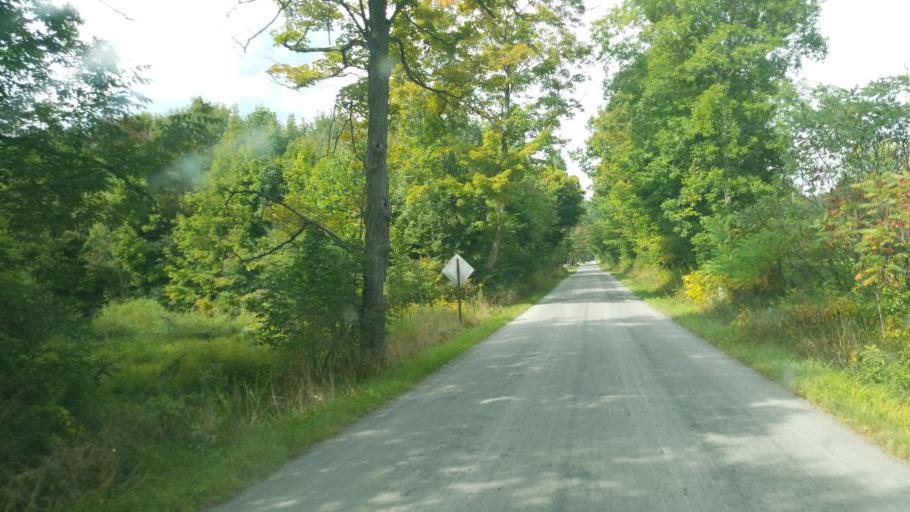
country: US
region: Pennsylvania
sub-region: Crawford County
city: Conneaut Lakeshore
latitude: 41.5254
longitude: -80.3169
